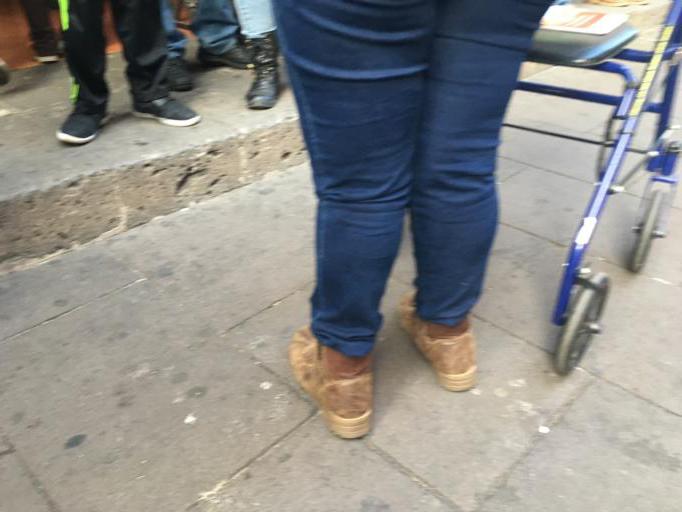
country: MX
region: Michoacan
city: Morelia
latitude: 19.7038
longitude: -101.1940
